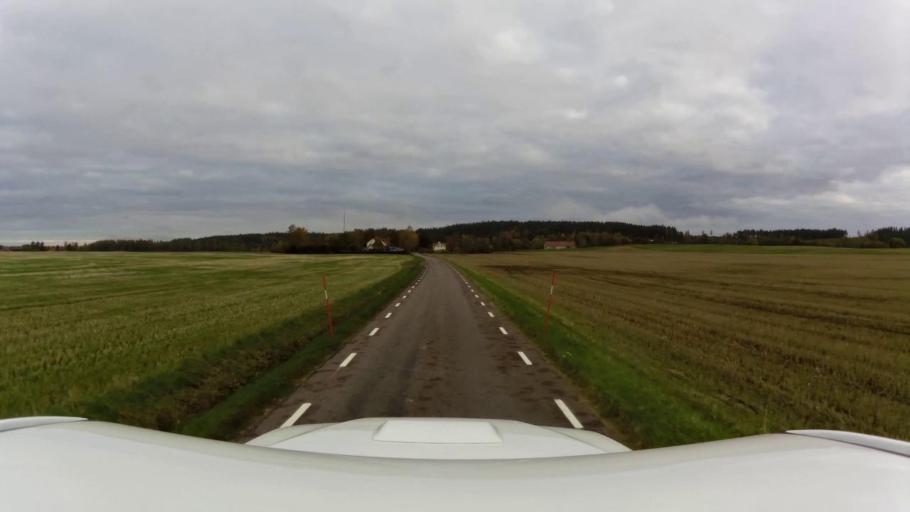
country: SE
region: OEstergoetland
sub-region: Linkopings Kommun
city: Ljungsbro
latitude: 58.5319
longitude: 15.4185
